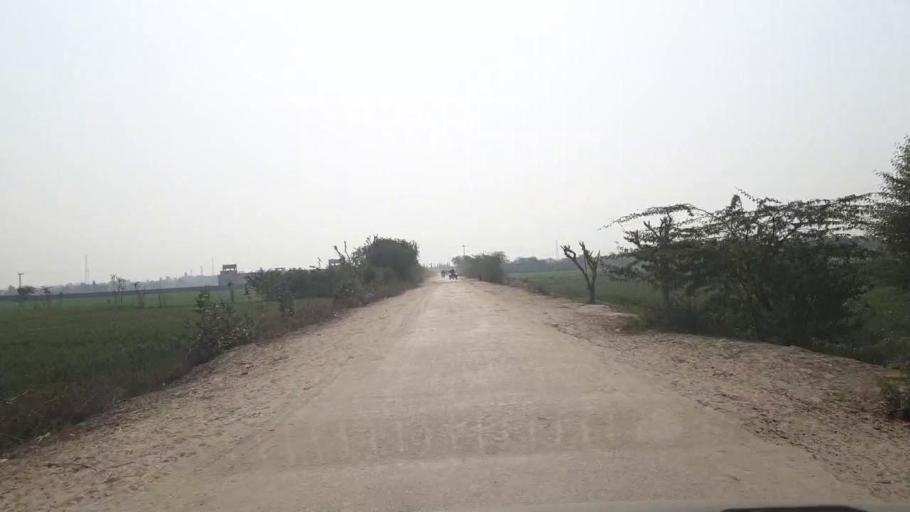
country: PK
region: Sindh
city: Bhit Shah
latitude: 25.8167
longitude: 68.4904
